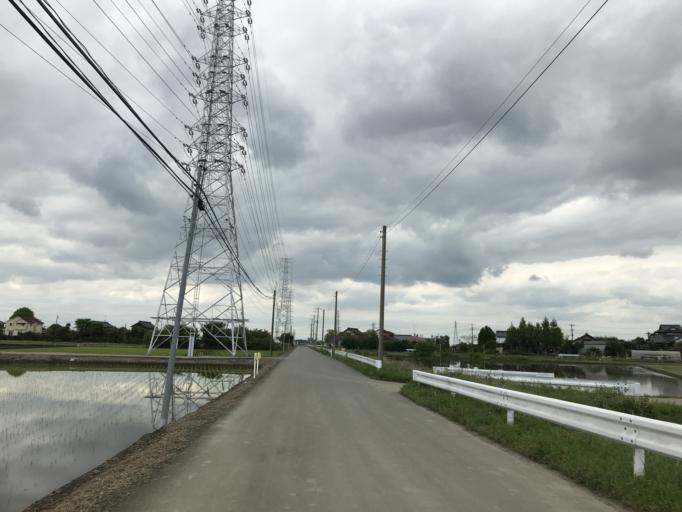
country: JP
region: Ibaraki
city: Mitsukaido
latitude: 36.0181
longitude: 140.0252
